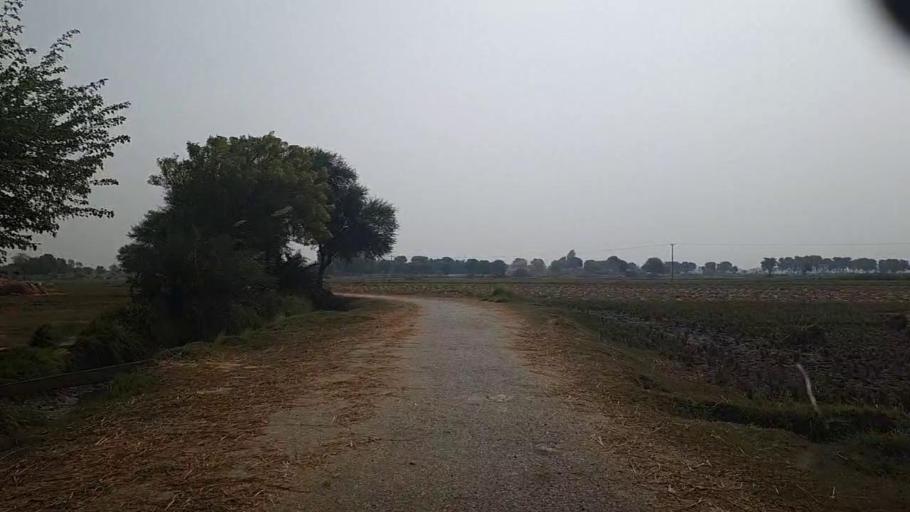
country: PK
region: Sindh
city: Kashmor
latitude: 28.3808
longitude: 69.4434
